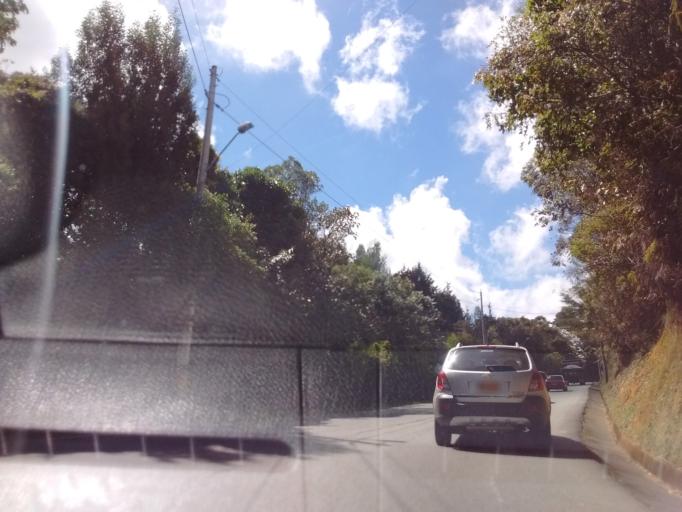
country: CO
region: Antioquia
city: Medellin
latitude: 6.2229
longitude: -75.5029
